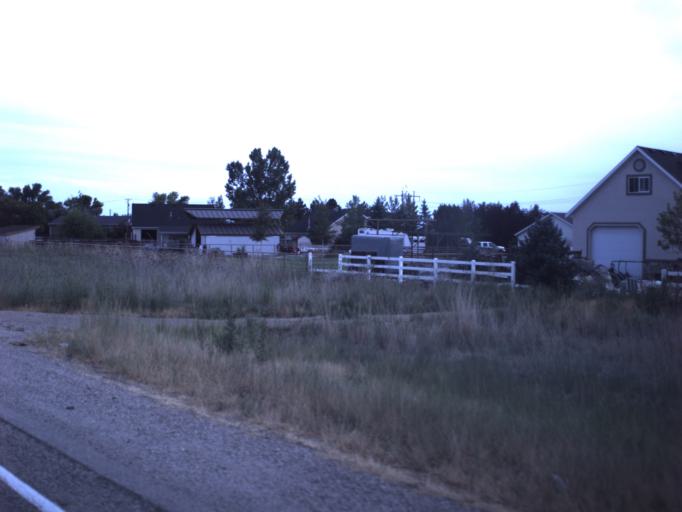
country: US
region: Utah
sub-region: Weber County
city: Farr West
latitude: 41.3157
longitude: -112.0281
